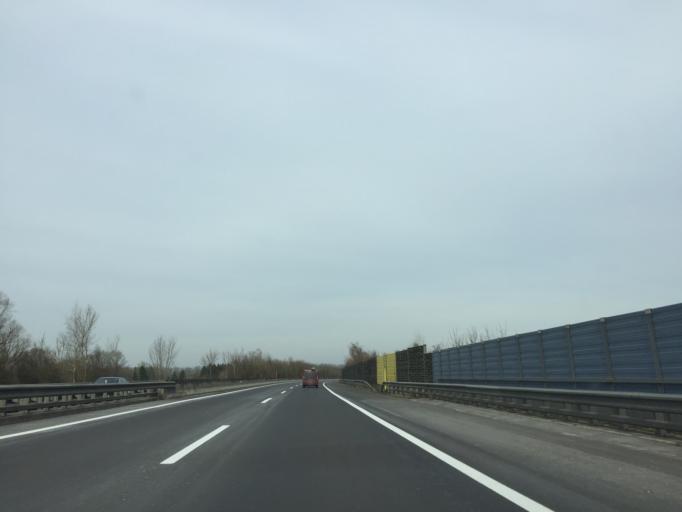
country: AT
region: Upper Austria
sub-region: Politischer Bezirk Scharding
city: Sankt Marienkirchen bei Schaerding
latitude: 48.3655
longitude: 13.4138
